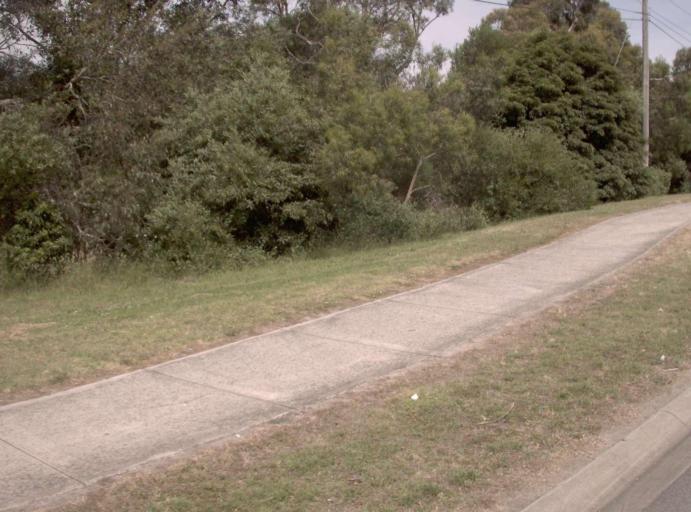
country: AU
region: Victoria
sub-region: Frankston
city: Frankston South
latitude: -38.1658
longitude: 145.1374
